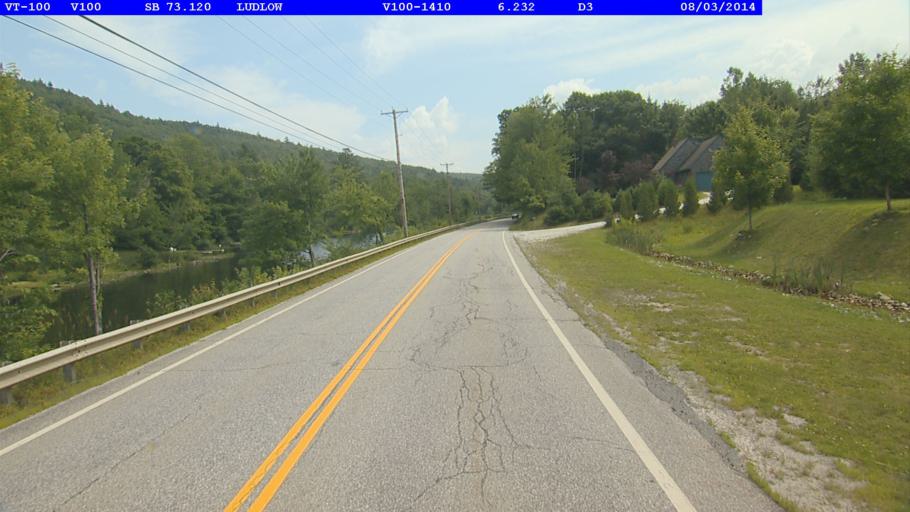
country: US
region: Vermont
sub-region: Windsor County
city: Chester
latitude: 43.4350
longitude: -72.6983
